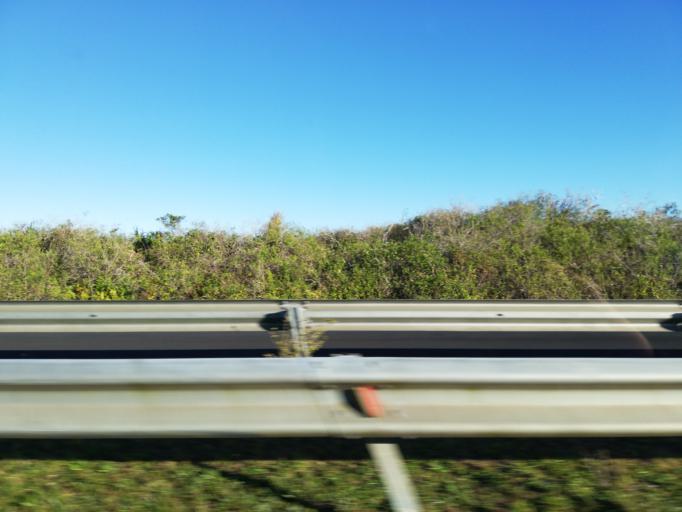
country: MU
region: Moka
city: La Dagotiere
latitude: -20.2573
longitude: 57.5301
